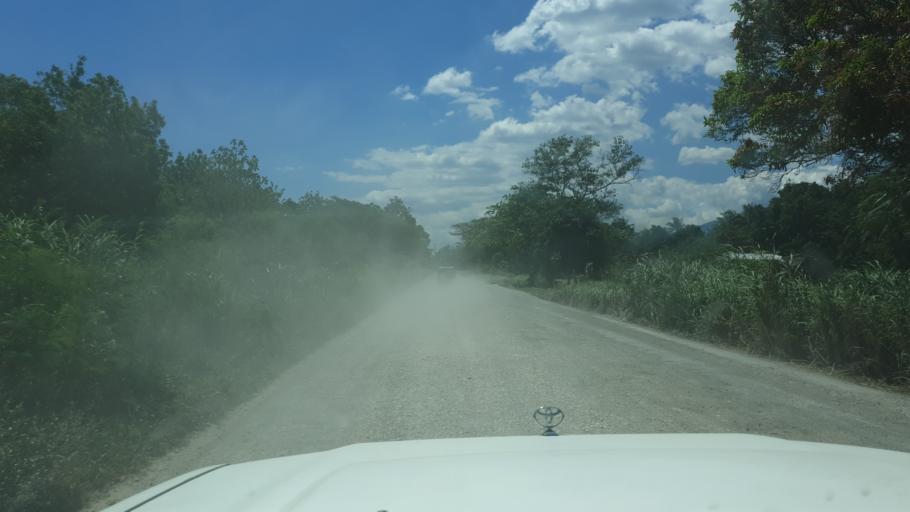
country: PG
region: Eastern Highlands
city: Goroka
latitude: -5.6768
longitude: 145.5018
